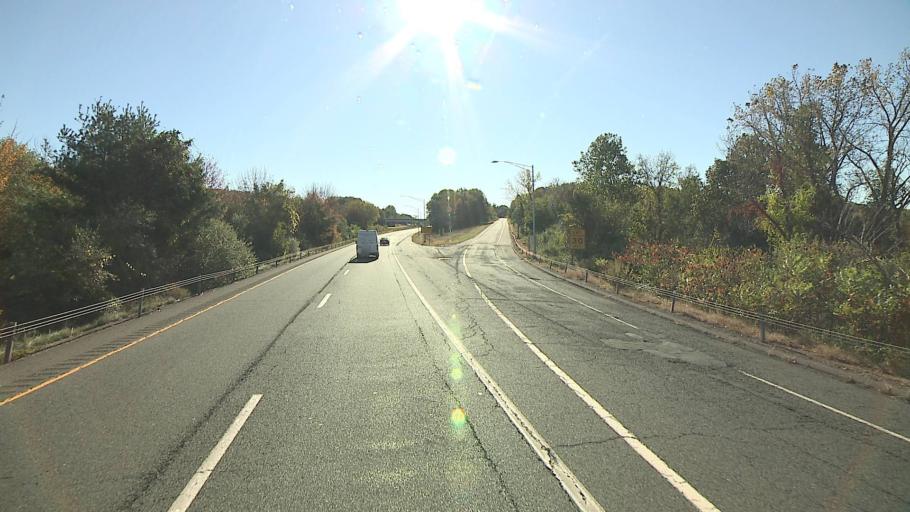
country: US
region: Connecticut
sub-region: New Haven County
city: Meriden
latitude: 41.5349
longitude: -72.7571
